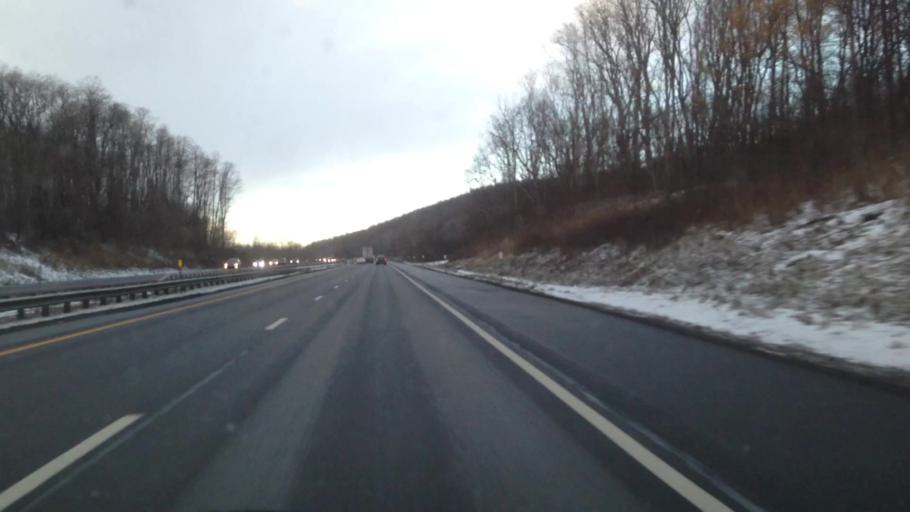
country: US
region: New York
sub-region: Herkimer County
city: Mohawk
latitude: 43.0206
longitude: -75.0169
